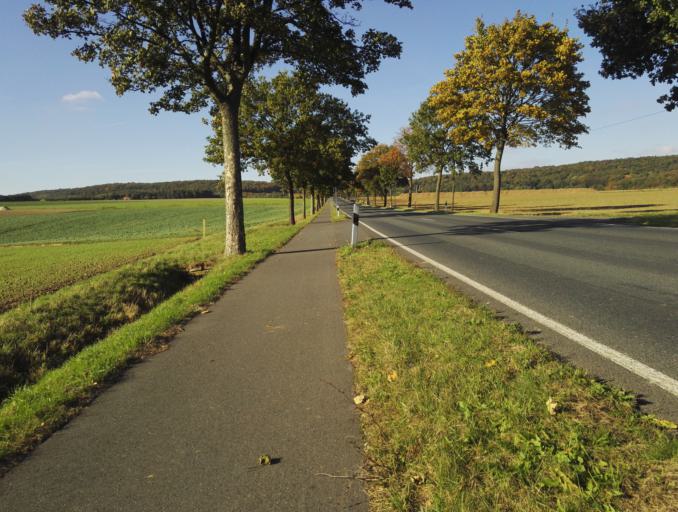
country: DE
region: Lower Saxony
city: Holle
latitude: 52.1133
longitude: 10.1055
